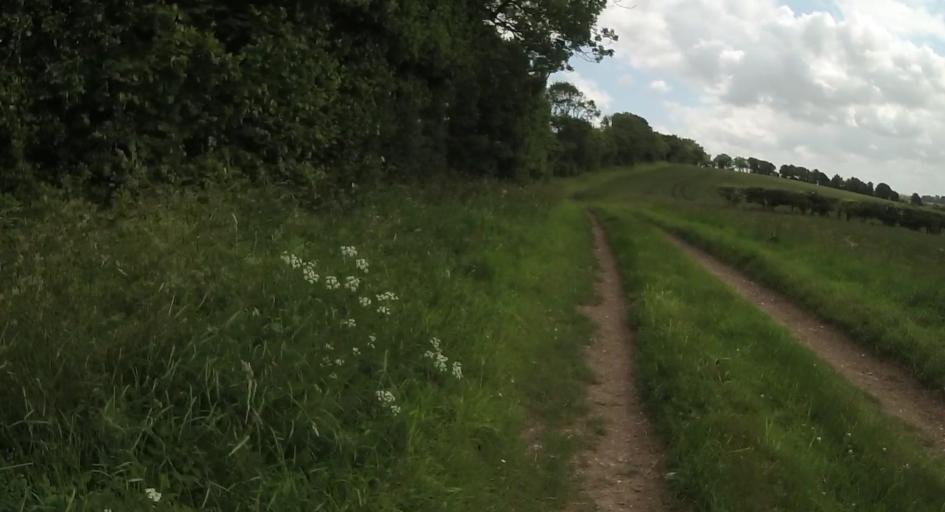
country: GB
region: England
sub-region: Hampshire
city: Basingstoke
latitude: 51.1732
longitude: -1.1654
